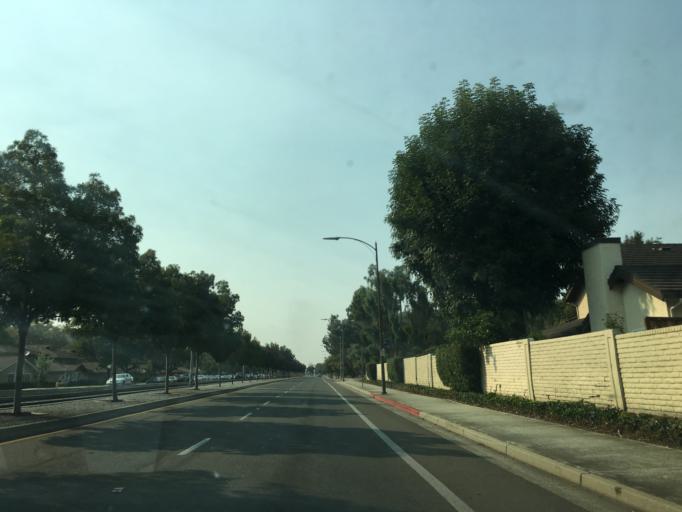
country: US
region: California
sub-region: Santa Clara County
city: Alum Rock
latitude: 37.3792
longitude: -121.8522
